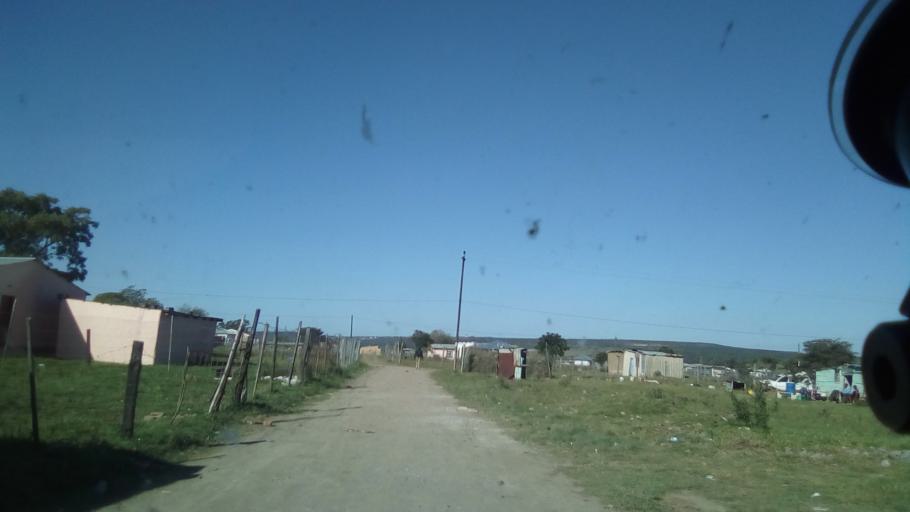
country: ZA
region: Eastern Cape
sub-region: Buffalo City Metropolitan Municipality
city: Bhisho
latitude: -32.8263
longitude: 27.3703
